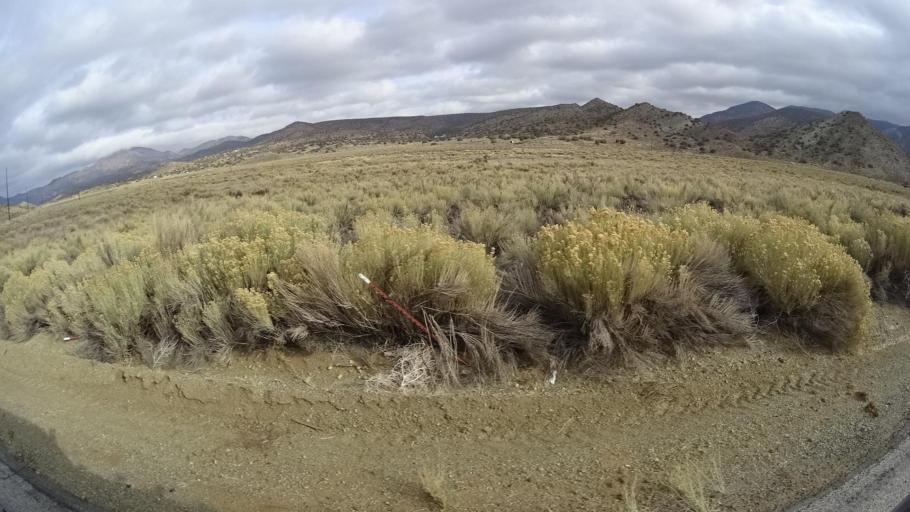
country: US
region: California
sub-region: Kern County
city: Tehachapi
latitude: 35.1510
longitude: -118.3187
